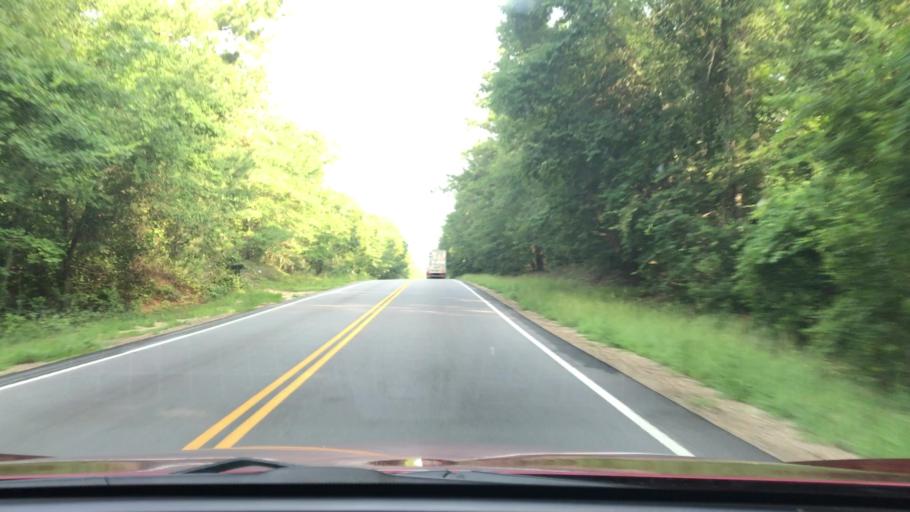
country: US
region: South Carolina
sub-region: Barnwell County
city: Blackville
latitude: 33.5453
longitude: -81.1504
